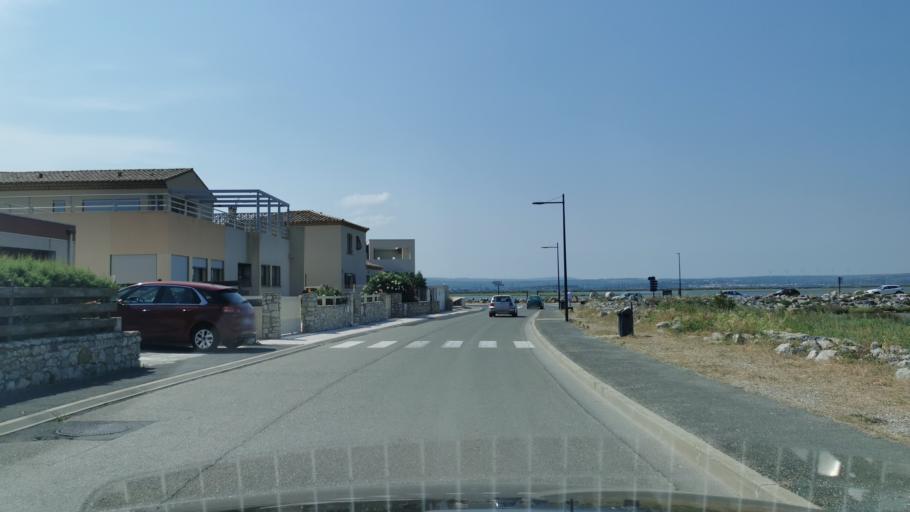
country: FR
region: Languedoc-Roussillon
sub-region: Departement de l'Aude
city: Leucate
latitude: 42.9376
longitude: 3.0270
